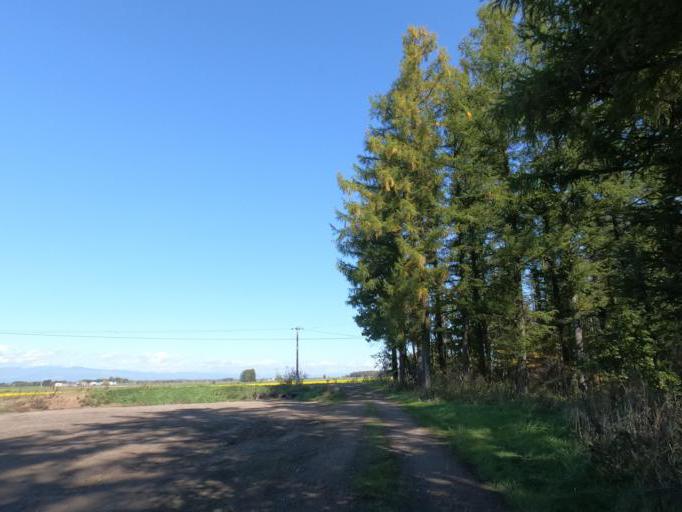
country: JP
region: Hokkaido
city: Otofuke
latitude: 43.0167
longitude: 143.2700
